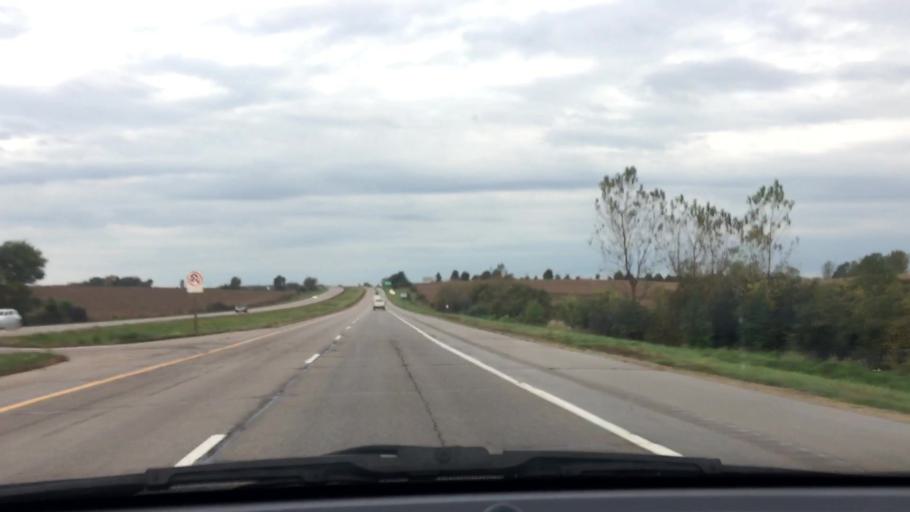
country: US
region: Wisconsin
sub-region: Rock County
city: Clinton
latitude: 42.5729
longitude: -88.8756
